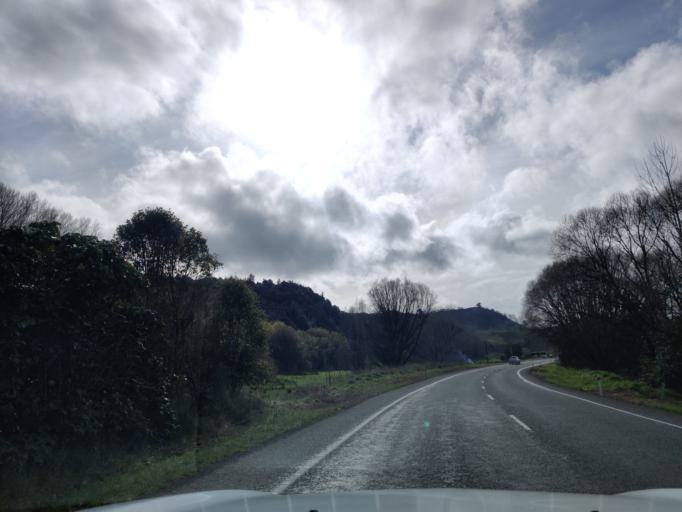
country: NZ
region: Manawatu-Wanganui
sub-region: Ruapehu District
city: Waiouru
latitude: -39.8406
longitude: 175.7426
